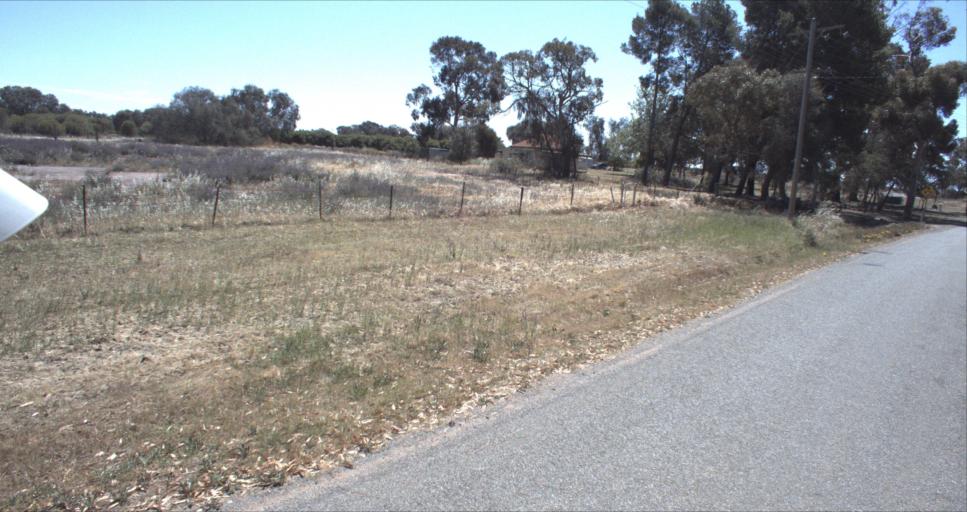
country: AU
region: New South Wales
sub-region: Leeton
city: Leeton
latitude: -34.5254
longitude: 146.3458
